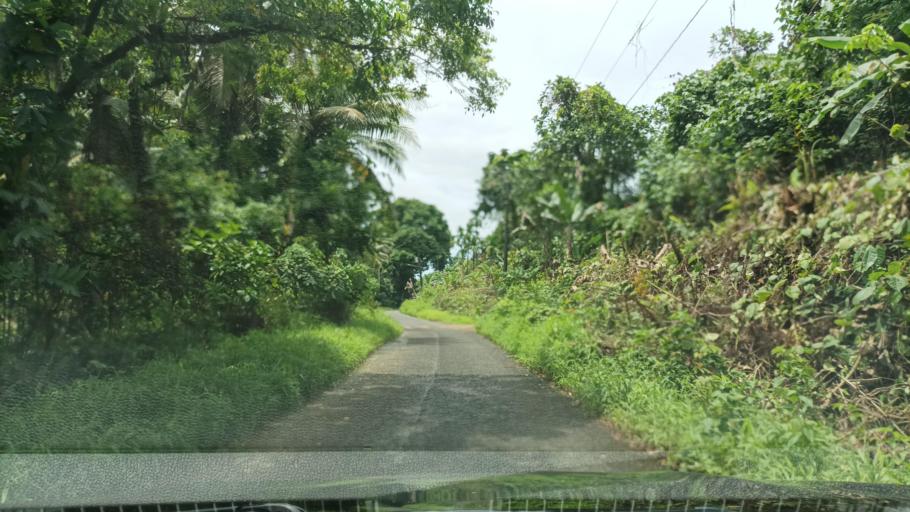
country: FM
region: Pohnpei
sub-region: Kolonia Municipality
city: Kolonia
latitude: 6.9635
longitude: 158.2246
